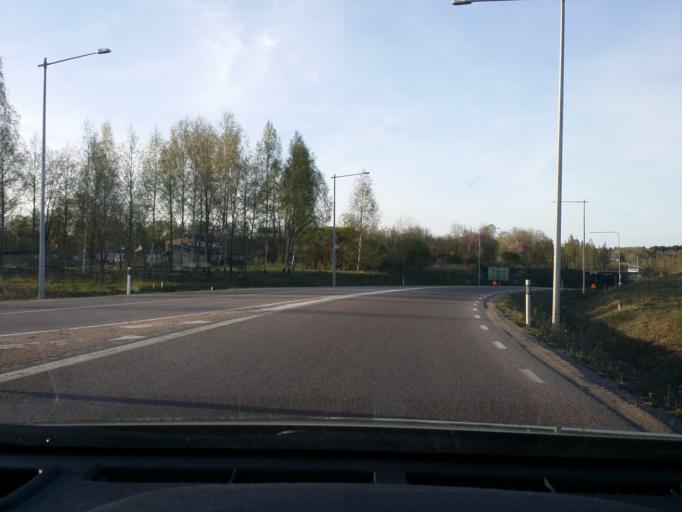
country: SE
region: Dalarna
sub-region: Avesta Kommun
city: Avesta
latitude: 60.1411
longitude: 16.1921
